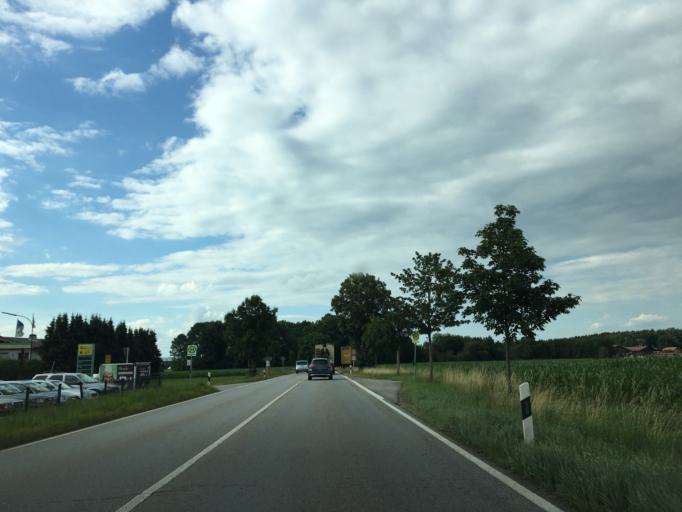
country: DE
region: Bavaria
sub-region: Upper Bavaria
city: Holzkirchen
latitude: 47.8713
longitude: 11.7180
